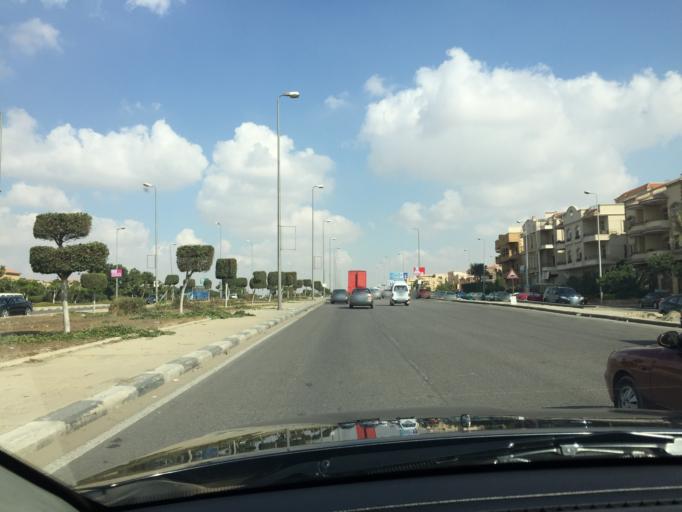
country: EG
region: Muhafazat al Qahirah
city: Cairo
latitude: 30.0173
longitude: 31.4471
